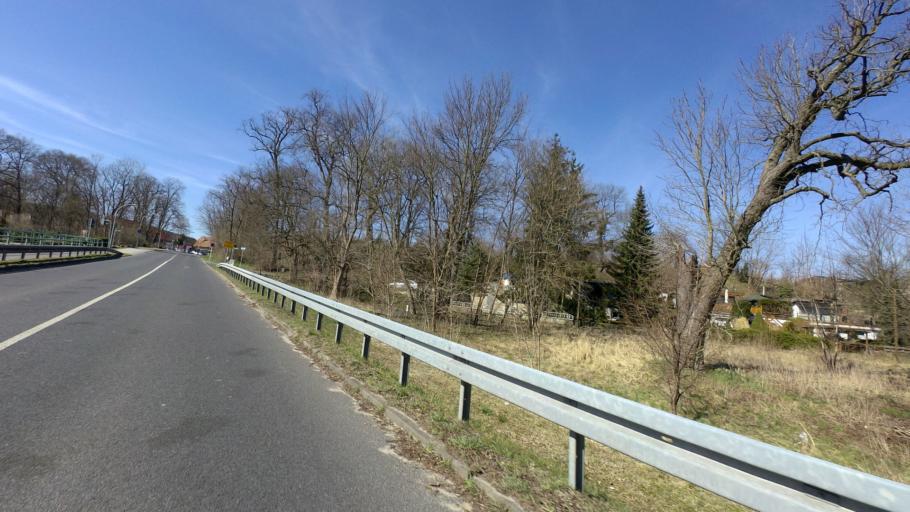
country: DE
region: Brandenburg
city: Furstenwalde
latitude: 52.4022
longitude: 14.0442
